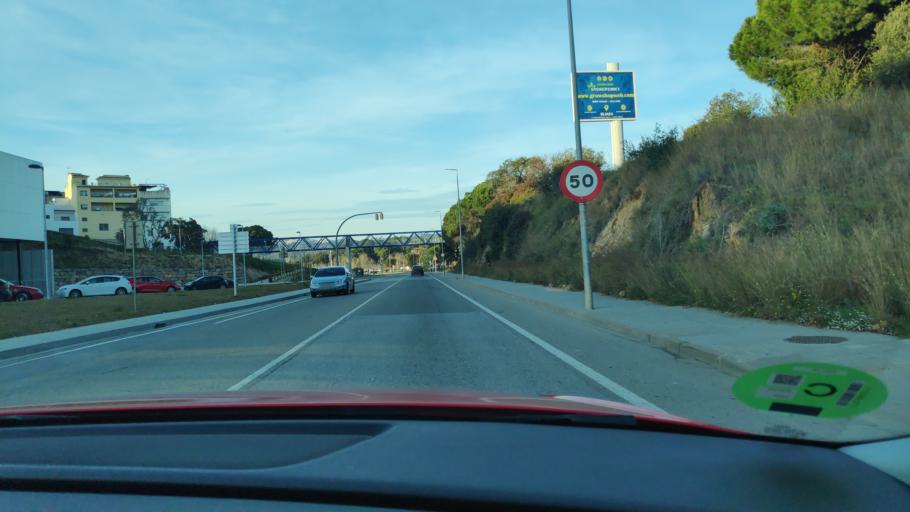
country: ES
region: Catalonia
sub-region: Provincia de Girona
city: Lloret de Mar
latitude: 41.7051
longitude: 2.8355
